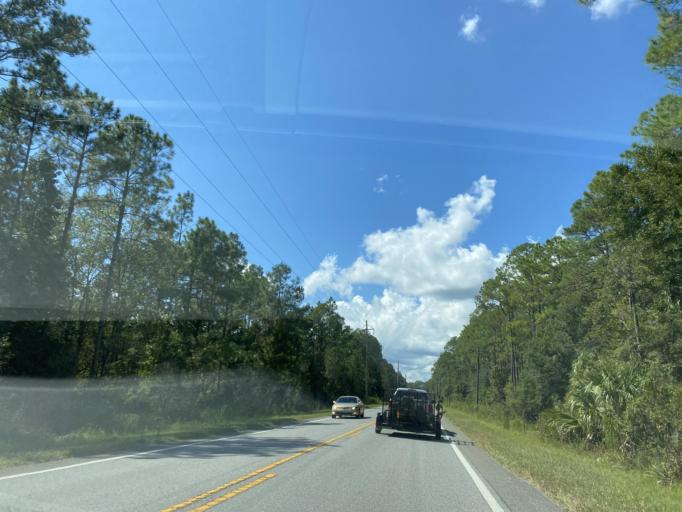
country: US
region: Florida
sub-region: Lake County
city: Umatilla
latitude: 28.9614
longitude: -81.5880
